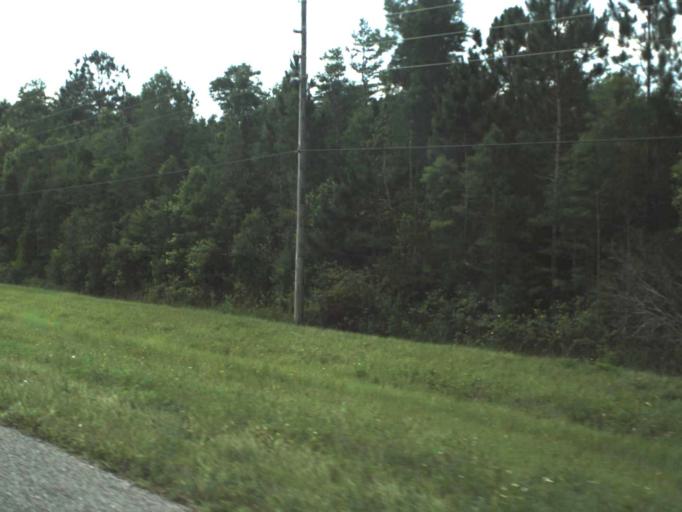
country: US
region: Florida
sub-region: Volusia County
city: Samsula-Spruce Creek
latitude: 29.0198
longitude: -81.1075
